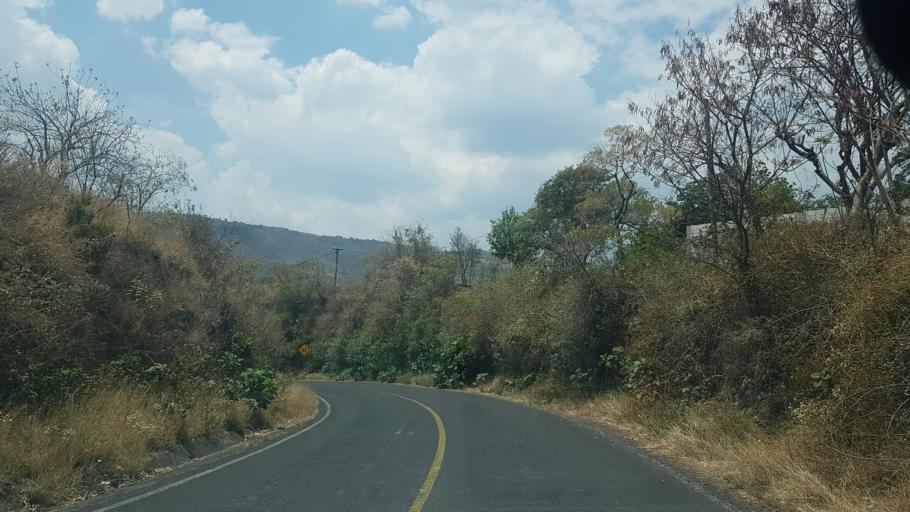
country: MX
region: Puebla
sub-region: Atzitzihuacan
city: Santiago Atzitzihuacan
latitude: 18.8422
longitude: -98.5851
